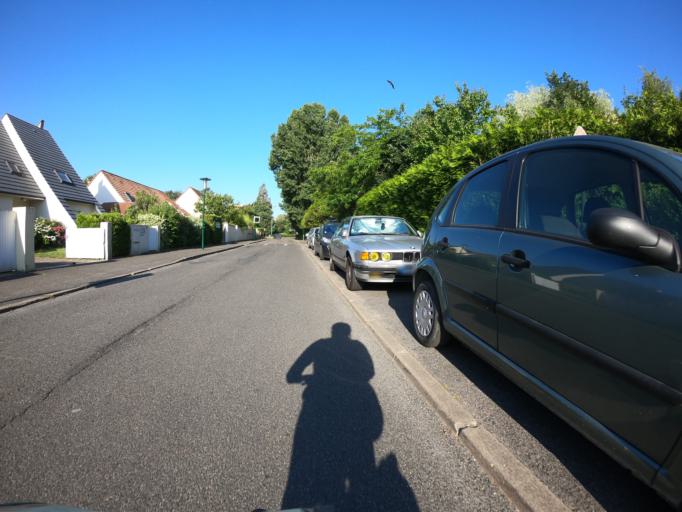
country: FR
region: Ile-de-France
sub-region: Departement de l'Essonne
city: Verrieres-le-Buisson
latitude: 48.7499
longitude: 2.2746
